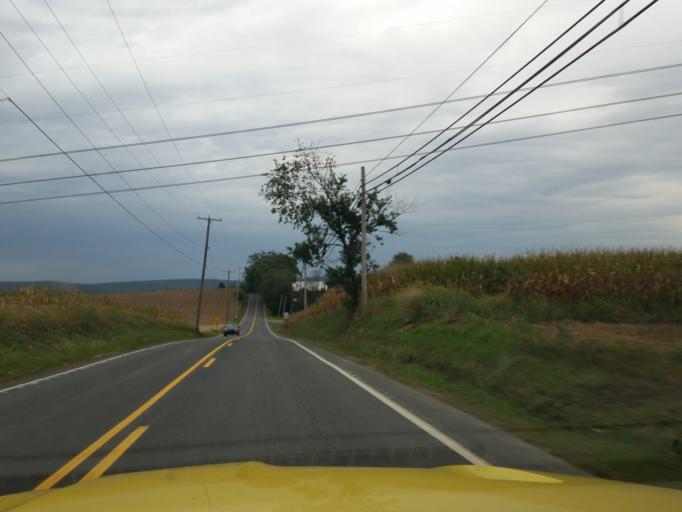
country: US
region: Pennsylvania
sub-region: Lebanon County
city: Myerstown
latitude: 40.4375
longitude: -76.3271
